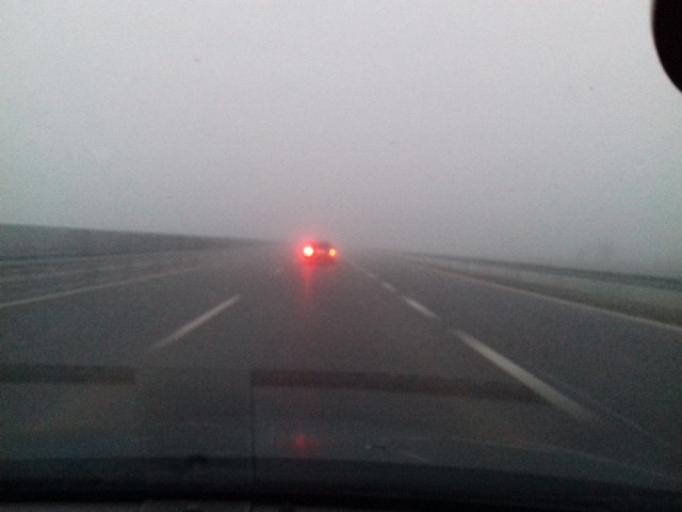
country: HU
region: Hajdu-Bihar
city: Hajdunanas
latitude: 47.8826
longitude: 21.4163
